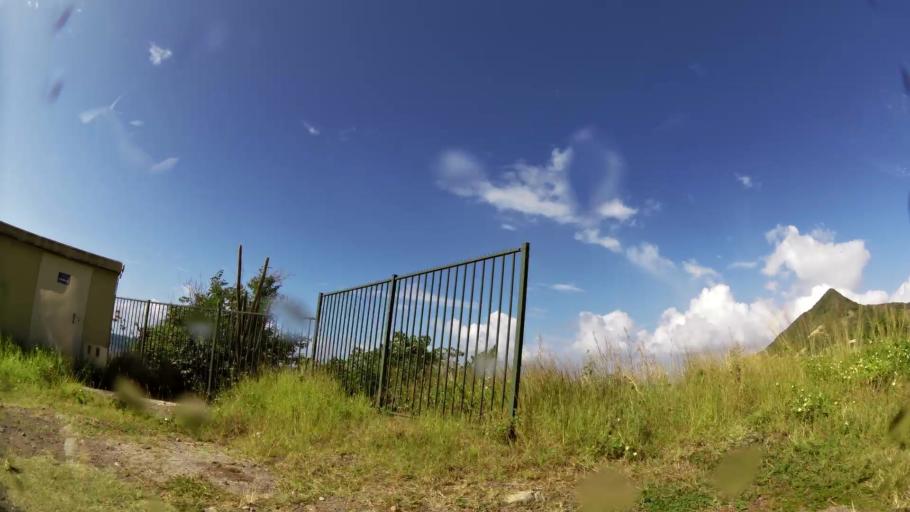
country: MQ
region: Martinique
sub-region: Martinique
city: Les Trois-Ilets
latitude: 14.4646
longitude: -61.0671
